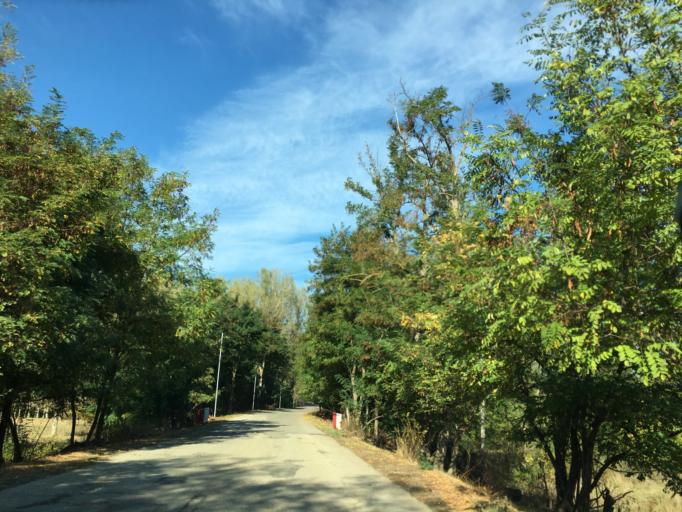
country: BG
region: Khaskovo
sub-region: Obshtina Ivaylovgrad
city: Ivaylovgrad
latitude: 41.3928
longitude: 26.1301
